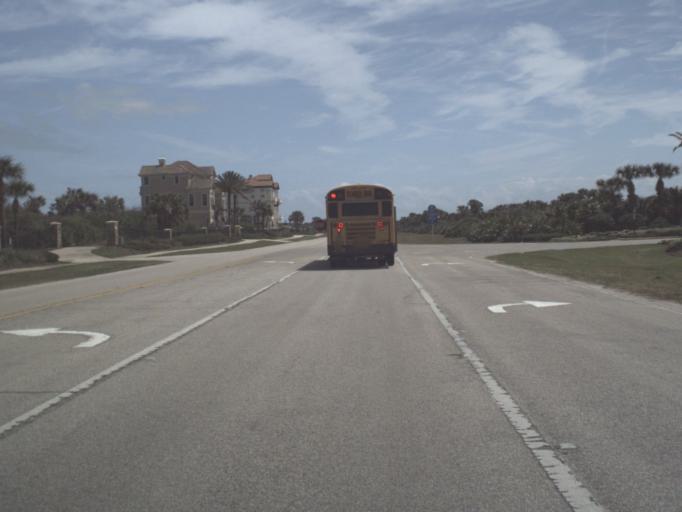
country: US
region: Florida
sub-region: Flagler County
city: Palm Coast
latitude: 29.5565
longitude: -81.1653
